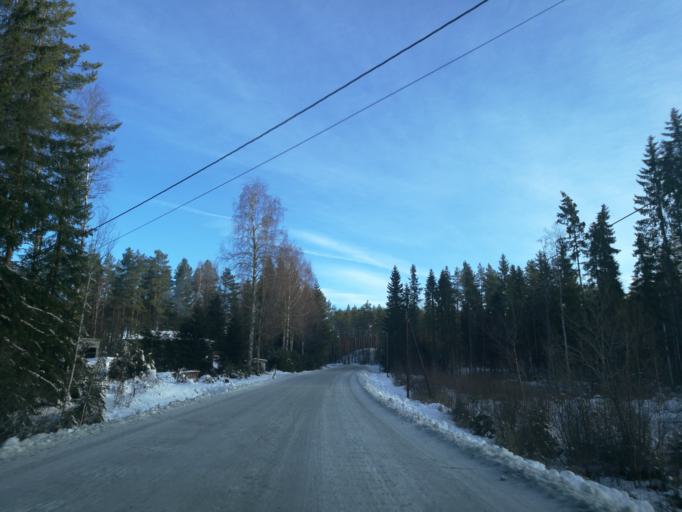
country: NO
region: Hedmark
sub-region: Grue
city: Kirkenaer
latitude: 60.3572
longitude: 12.3422
